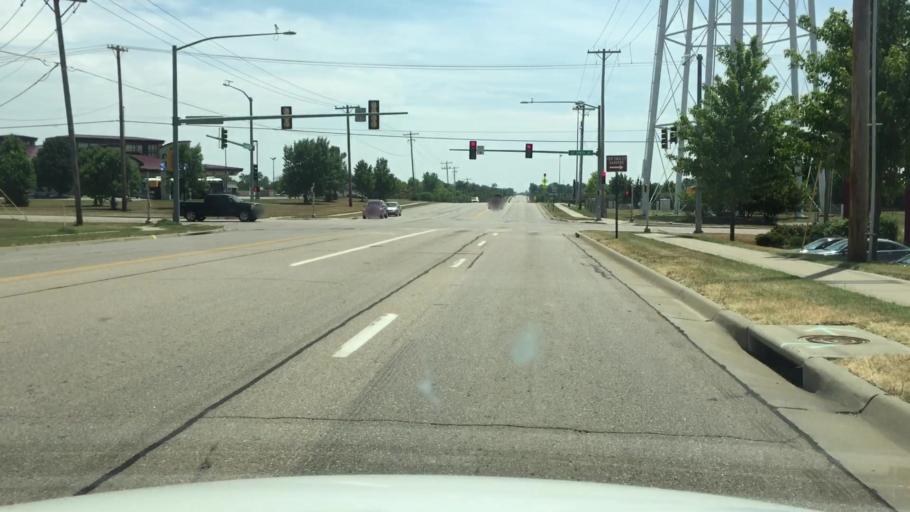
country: US
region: Kansas
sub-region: Shawnee County
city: Topeka
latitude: 39.0157
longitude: -95.6143
